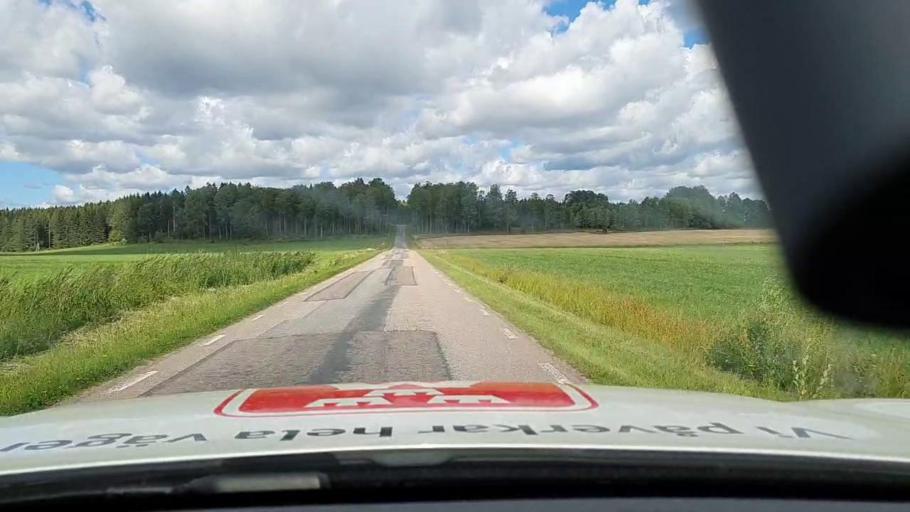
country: SE
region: Vaestra Goetaland
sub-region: Karlsborgs Kommun
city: Molltorp
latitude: 58.6044
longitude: 14.3142
